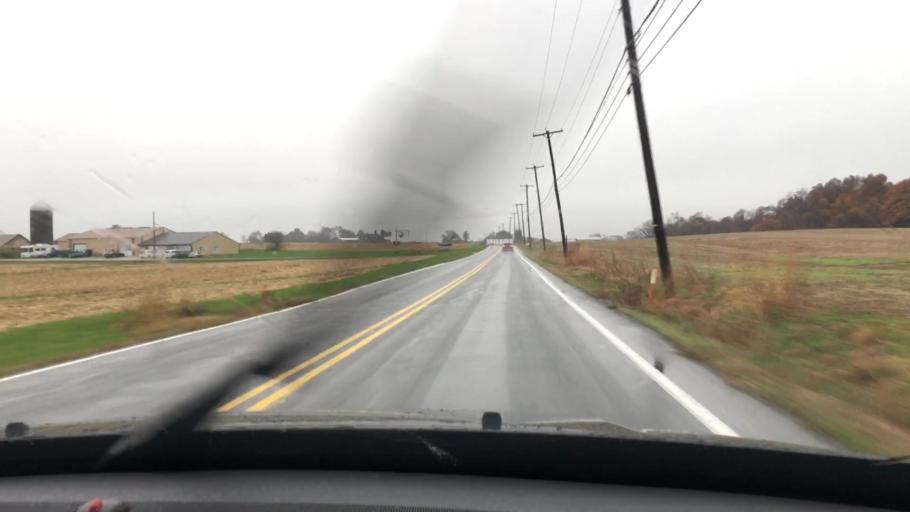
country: US
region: Pennsylvania
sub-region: York County
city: Stewartstown
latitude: 39.7306
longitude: -76.5133
